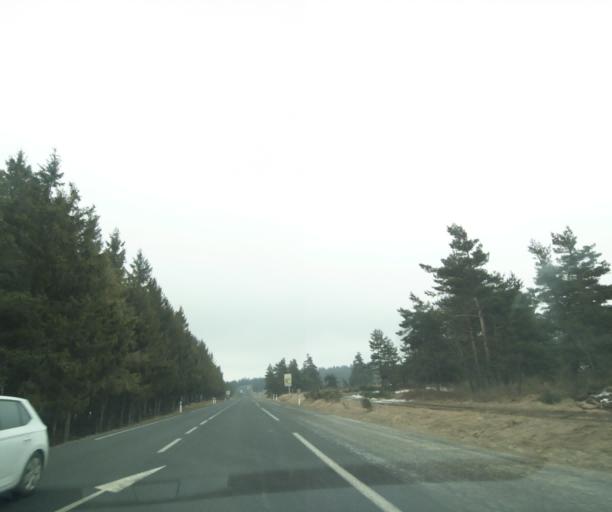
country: FR
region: Languedoc-Roussillon
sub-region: Departement de la Lozere
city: Langogne
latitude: 44.7529
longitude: 3.9568
